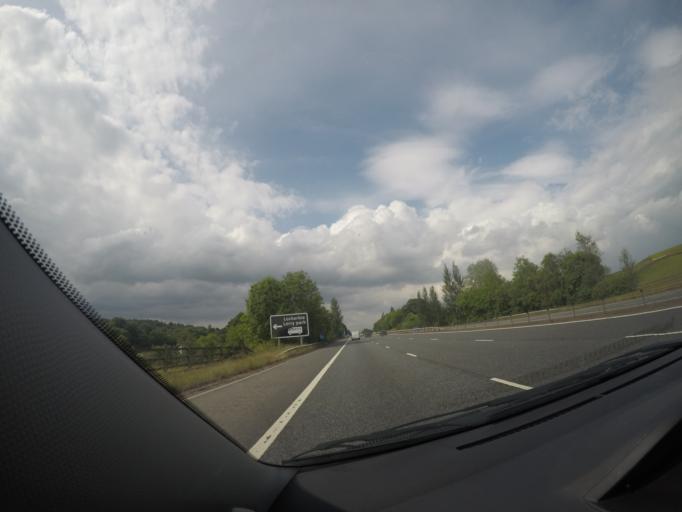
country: GB
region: Scotland
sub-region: Dumfries and Galloway
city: Lochmaben
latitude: 55.2114
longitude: -3.4130
